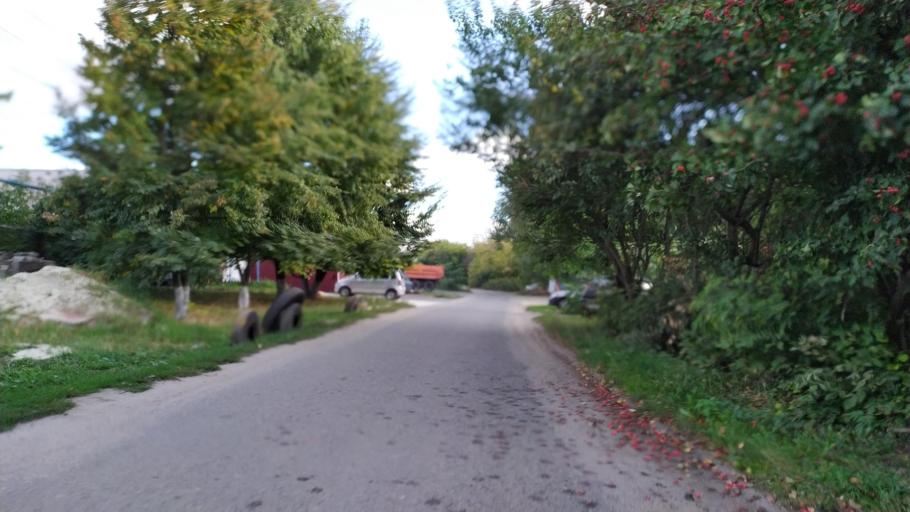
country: RU
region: Kursk
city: Kursk
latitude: 51.6292
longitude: 36.1538
